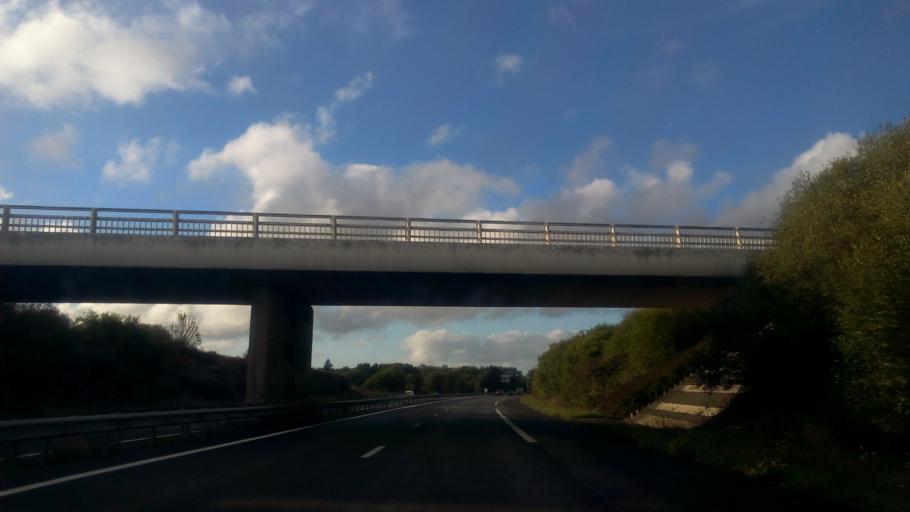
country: FR
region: Pays de la Loire
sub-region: Departement de la Loire-Atlantique
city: Pontchateau
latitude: 47.4228
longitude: -2.0548
